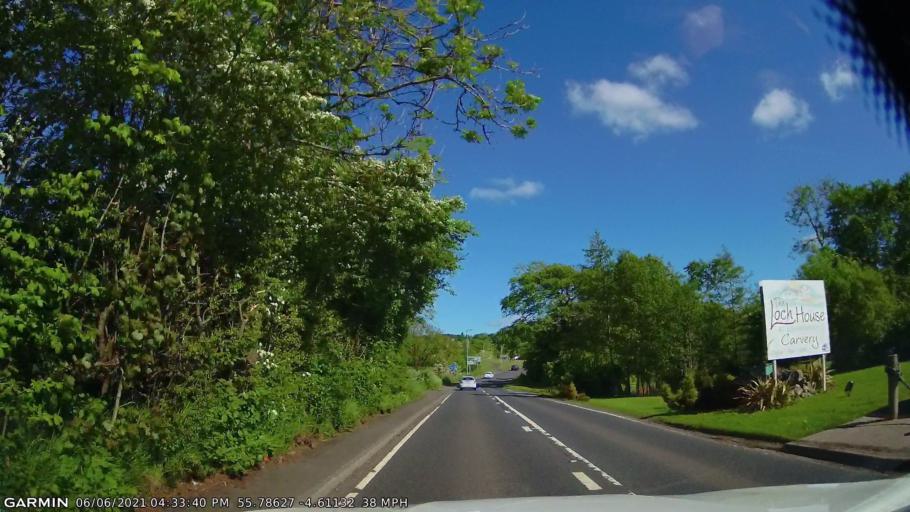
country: GB
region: Scotland
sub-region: Renfrewshire
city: Lochwinnoch
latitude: 55.7863
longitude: -4.6113
